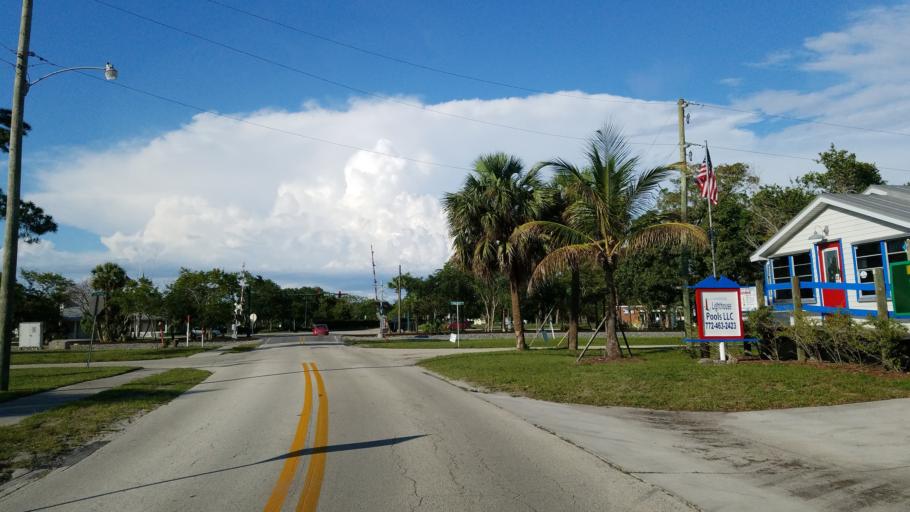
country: US
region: Florida
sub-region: Martin County
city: Port Salerno
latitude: 27.1461
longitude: -80.1995
